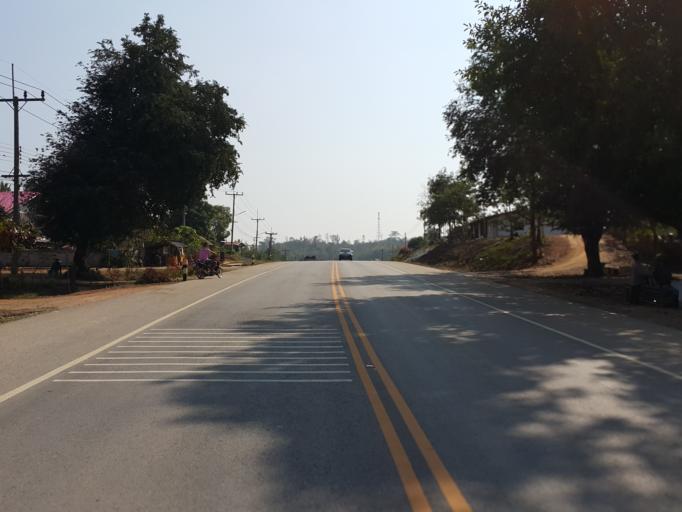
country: TH
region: Lampang
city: Mueang Pan
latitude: 18.8994
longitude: 99.6062
